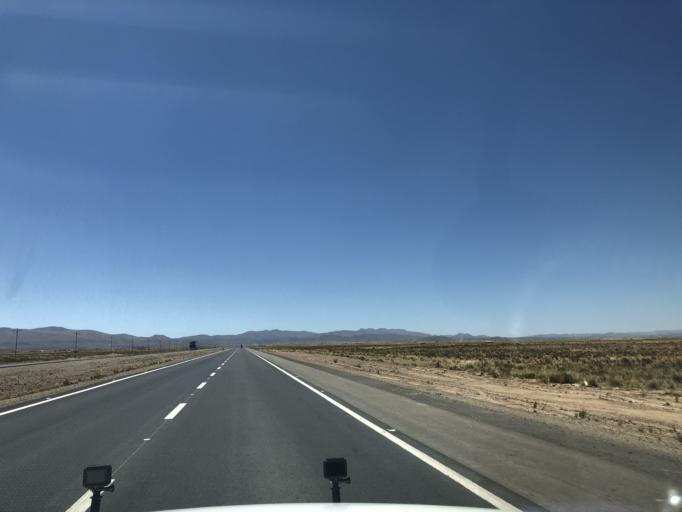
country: BO
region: La Paz
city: Colquiri
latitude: -17.6508
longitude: -67.1812
